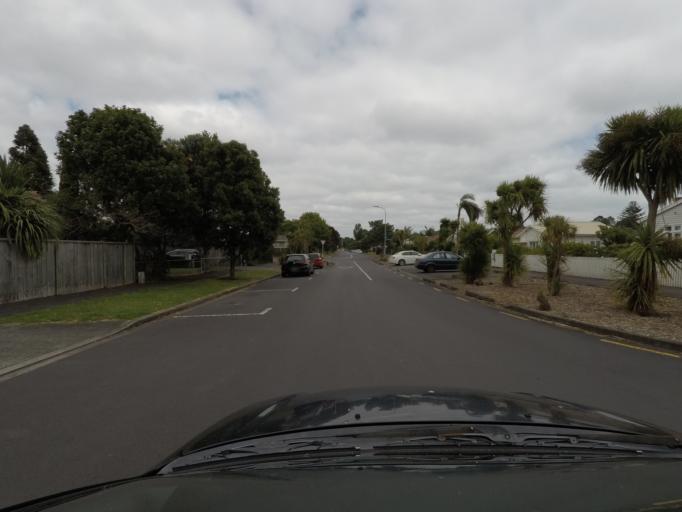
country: NZ
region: Auckland
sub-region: Auckland
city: Auckland
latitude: -36.8675
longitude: 174.7341
